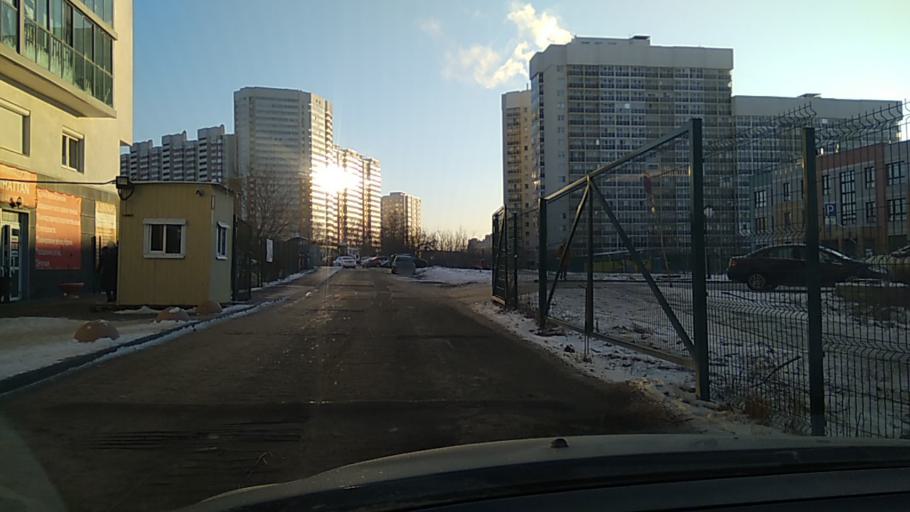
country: RU
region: Sverdlovsk
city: Yekaterinburg
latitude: 56.7823
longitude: 60.6663
